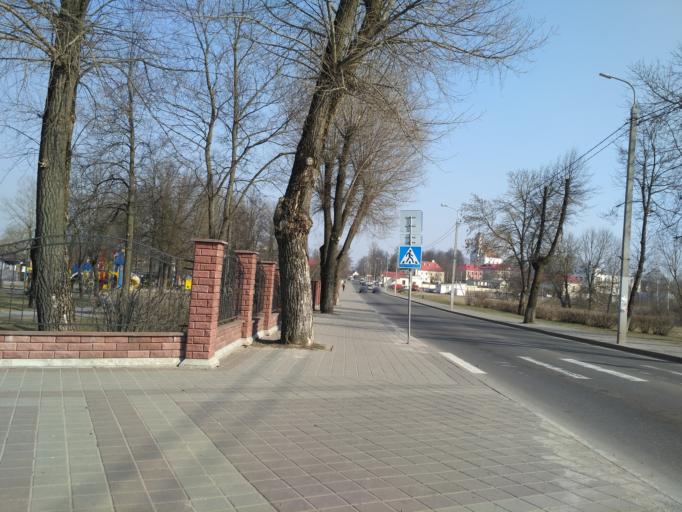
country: BY
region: Minsk
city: Zaslawye
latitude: 54.0062
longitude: 27.2855
